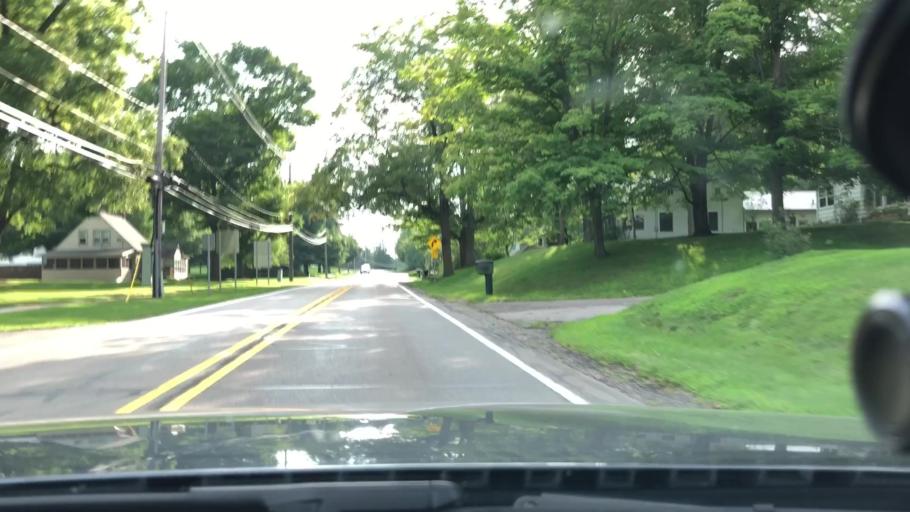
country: US
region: Michigan
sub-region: Washtenaw County
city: Manchester
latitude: 42.1453
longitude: -84.0498
